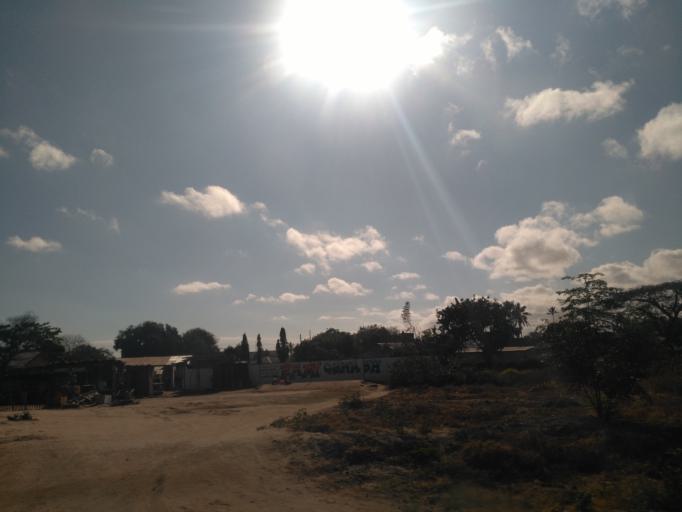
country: TZ
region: Dodoma
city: Dodoma
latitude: -6.1853
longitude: 35.7325
